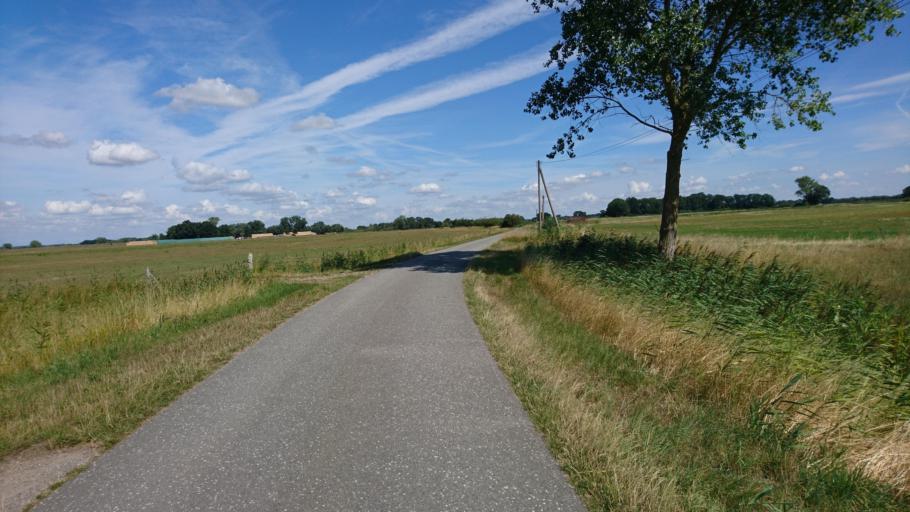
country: DE
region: Lower Saxony
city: Bleckede
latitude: 53.3068
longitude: 10.7480
